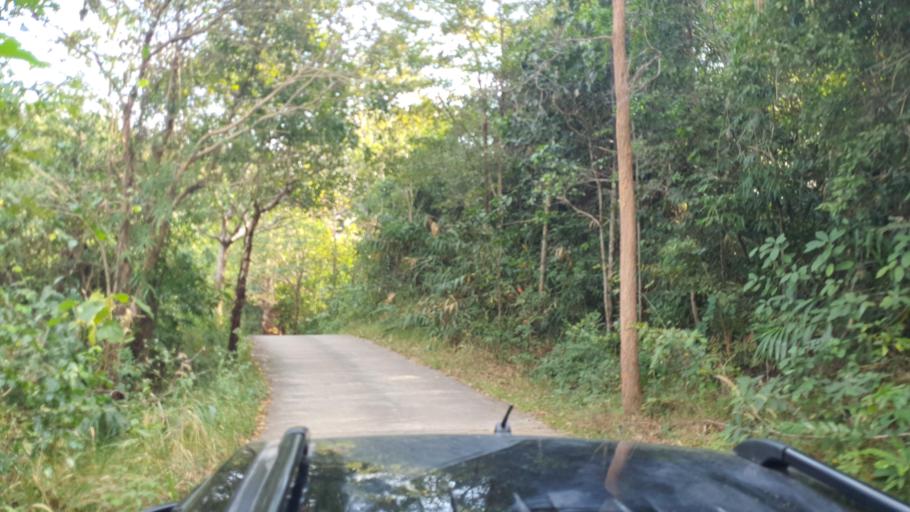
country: TH
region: Changwat Bueng Kan
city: Si Wilai
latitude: 18.2703
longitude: 103.7974
